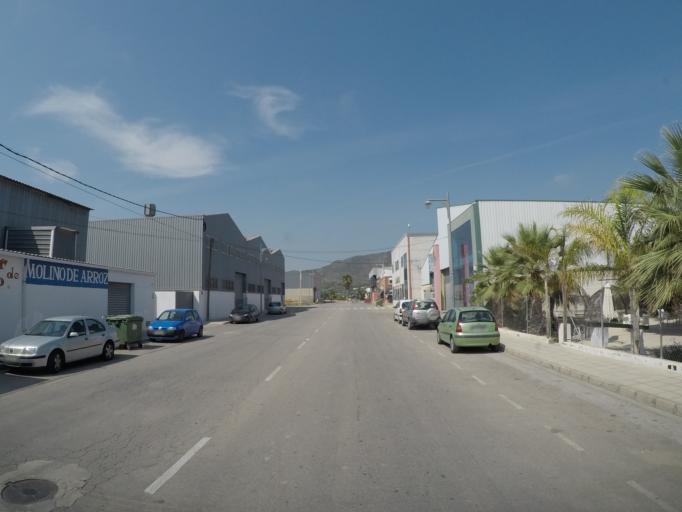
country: ES
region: Valencia
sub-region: Provincia de Alicante
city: Pego
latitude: 38.8471
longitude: -0.1129
